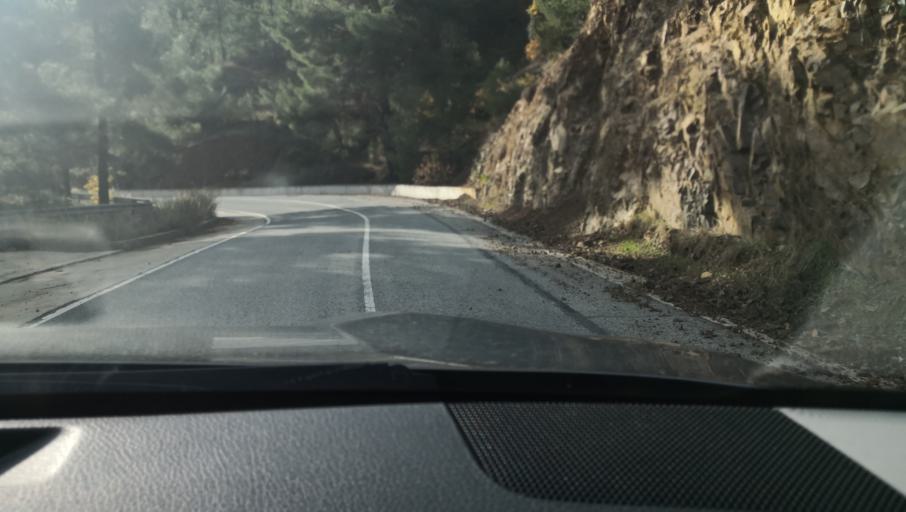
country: CY
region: Lefkosia
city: Lefka
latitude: 35.0198
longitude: 32.7257
